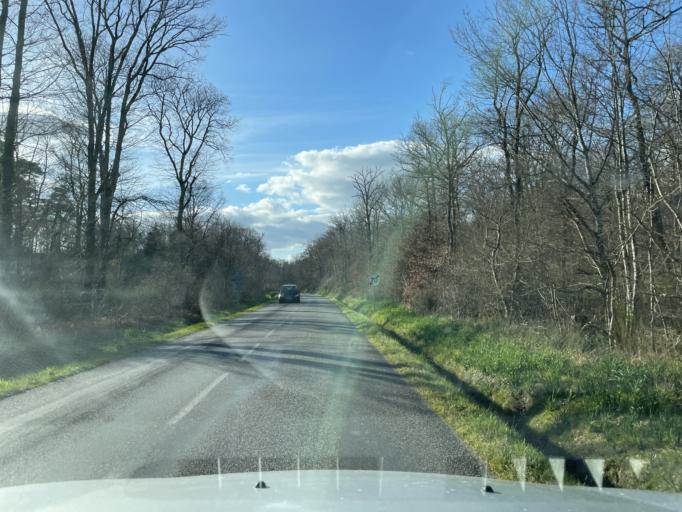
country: FR
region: Midi-Pyrenees
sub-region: Departement de la Haute-Garonne
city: Leguevin
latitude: 43.6157
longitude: 1.1986
